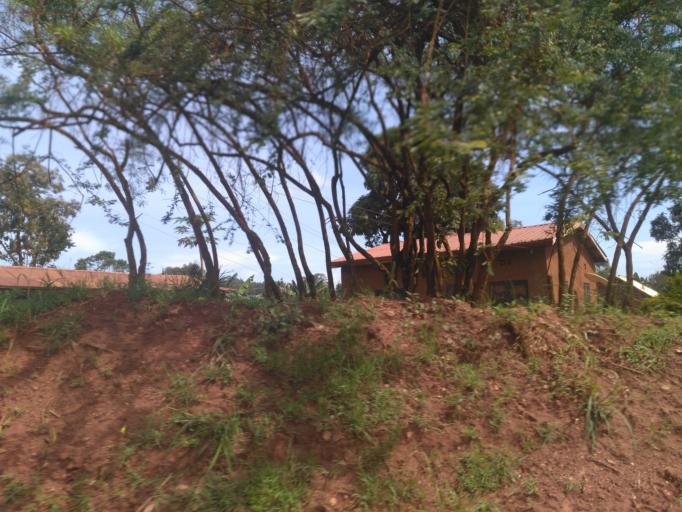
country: UG
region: Central Region
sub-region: Wakiso District
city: Kireka
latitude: 0.4413
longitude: 32.5890
